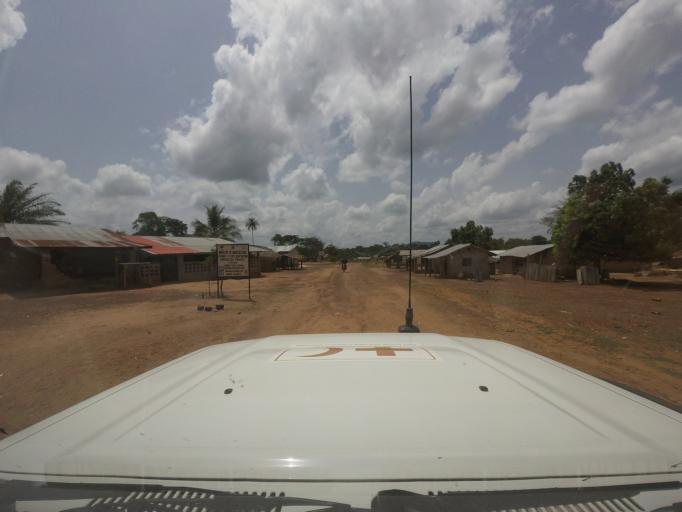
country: GN
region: Nzerekore
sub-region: Yomou
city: Yomou
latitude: 7.2865
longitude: -9.2160
